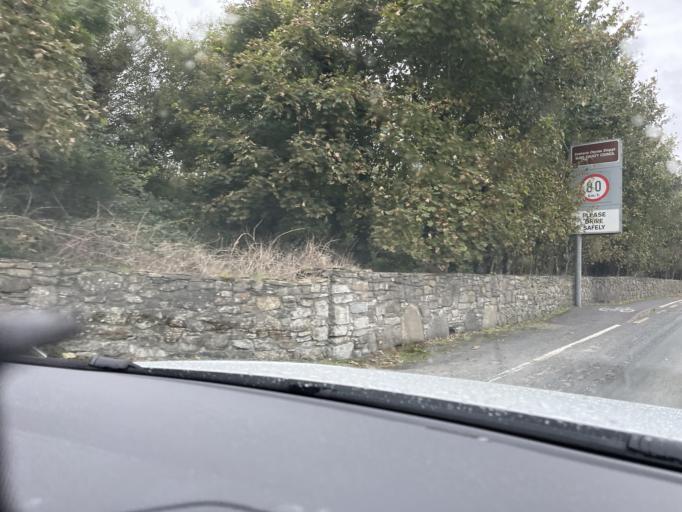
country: IE
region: Connaught
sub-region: Sligo
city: Strandhill
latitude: 54.3057
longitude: -8.5455
